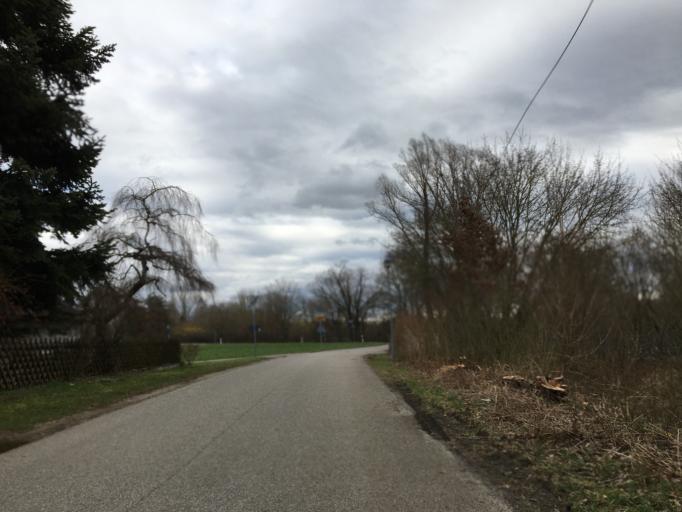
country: DE
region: Bavaria
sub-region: Upper Bavaria
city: Fuerstenfeldbruck
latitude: 48.1819
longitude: 11.2225
